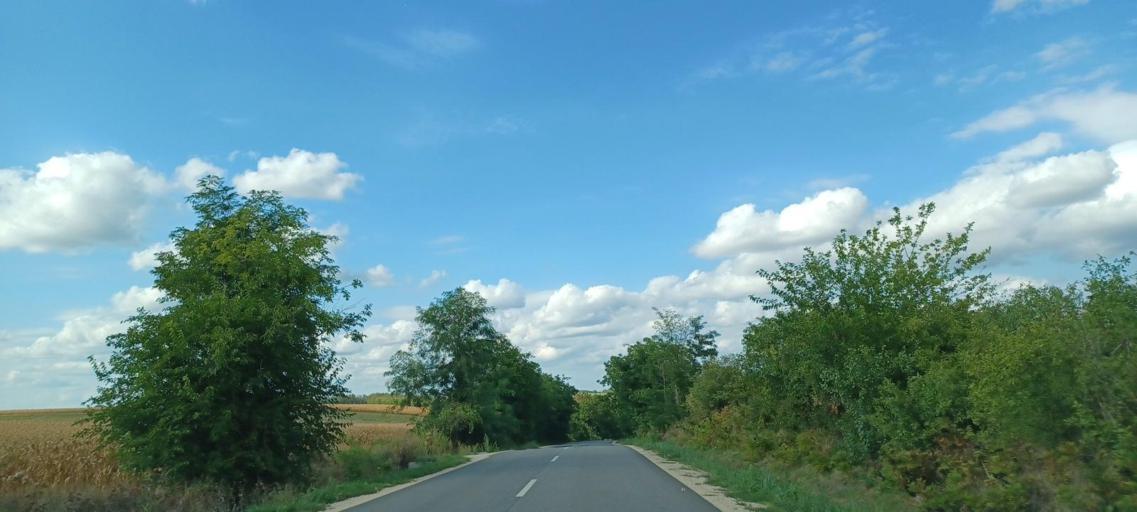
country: HU
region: Tolna
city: Zomba
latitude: 46.4719
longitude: 18.5957
